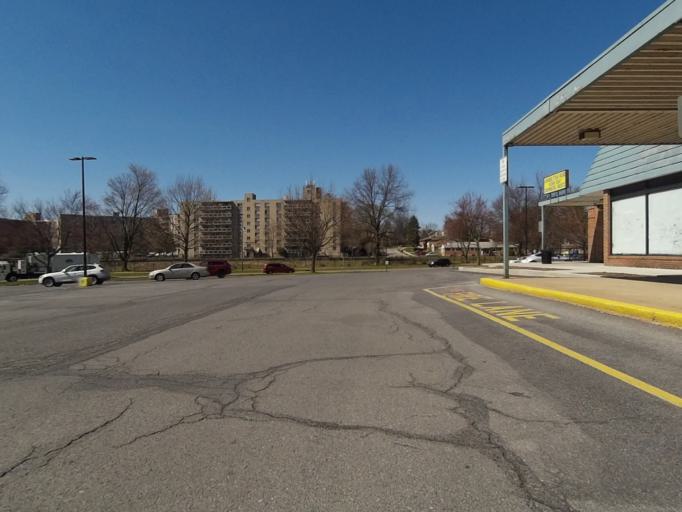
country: US
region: Pennsylvania
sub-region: Centre County
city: State College
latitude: 40.7837
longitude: -77.8522
